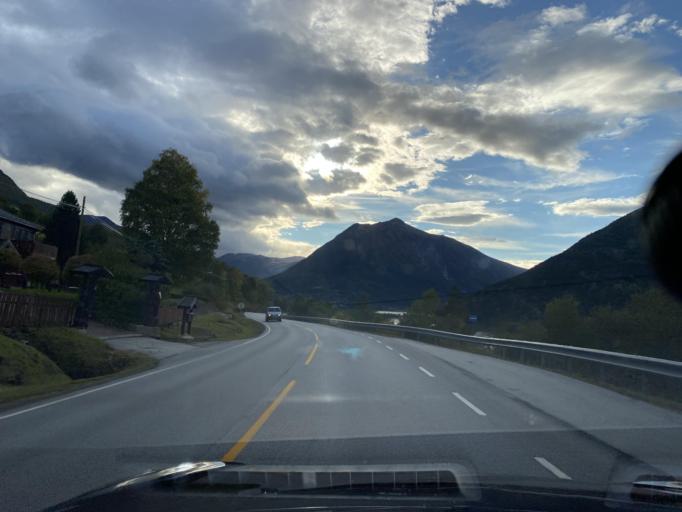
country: NO
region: Oppland
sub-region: Lom
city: Fossbergom
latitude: 61.8521
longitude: 8.6176
